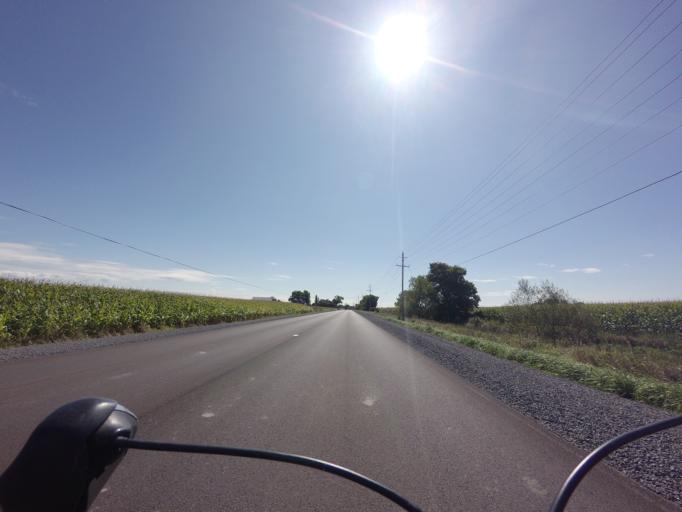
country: CA
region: Ontario
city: Bells Corners
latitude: 45.2242
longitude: -75.8576
